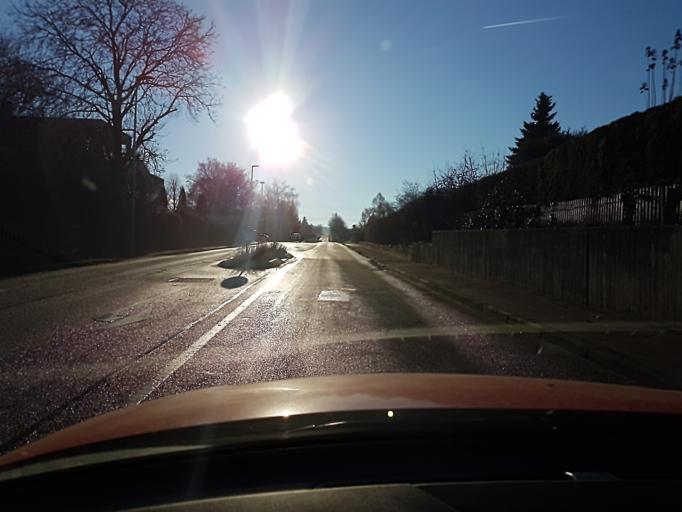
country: DE
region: Baden-Wuerttemberg
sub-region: Regierungsbezirk Stuttgart
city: Bonnigheim
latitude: 49.0366
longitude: 9.0908
